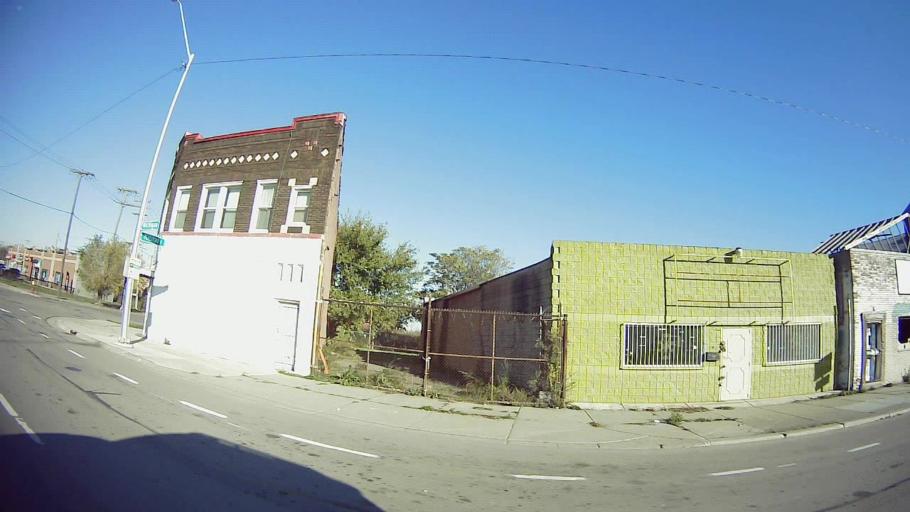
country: US
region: Michigan
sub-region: Wayne County
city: Dearborn
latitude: 42.3312
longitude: -83.1183
